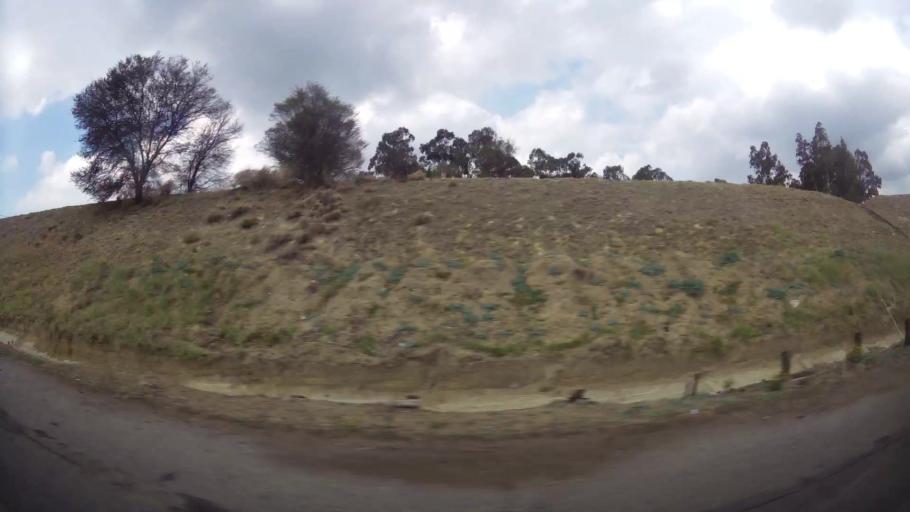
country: ZA
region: Gauteng
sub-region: Sedibeng District Municipality
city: Vereeniging
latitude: -26.6973
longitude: 27.9361
